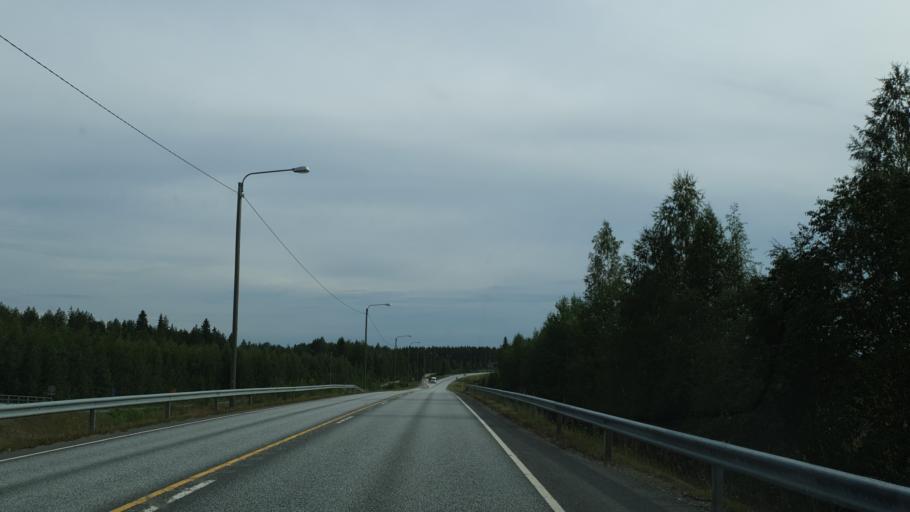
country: FI
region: North Karelia
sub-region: Joensuu
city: Kontiolahti
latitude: 62.7351
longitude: 29.8691
